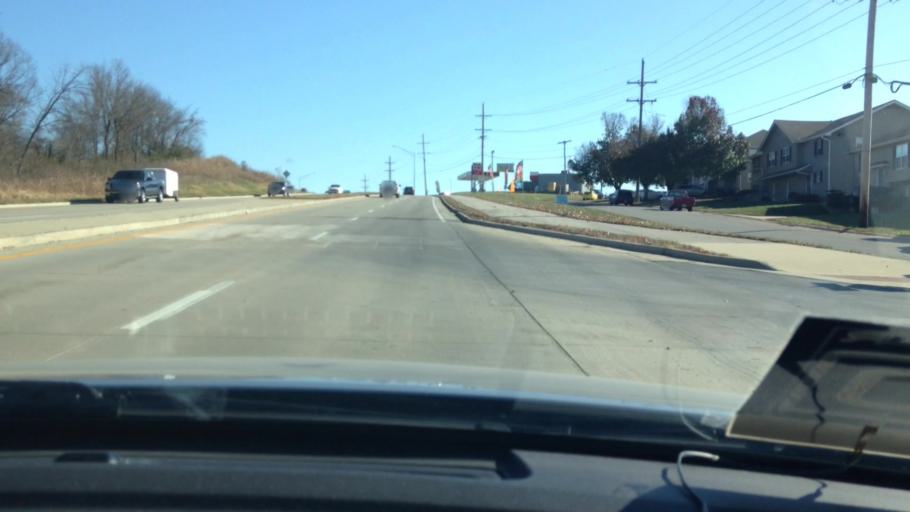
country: US
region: Missouri
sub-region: Platte County
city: Weatherby Lake
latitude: 39.2103
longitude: -94.7115
